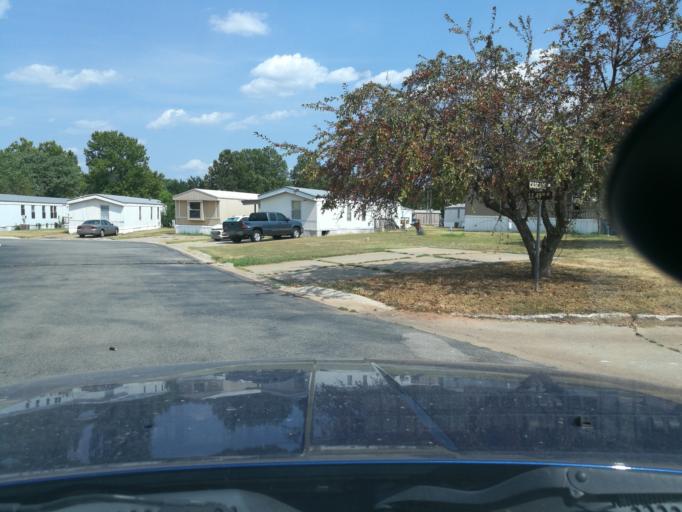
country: US
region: Oklahoma
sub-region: Oklahoma County
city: Del City
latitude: 35.4166
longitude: -97.4721
